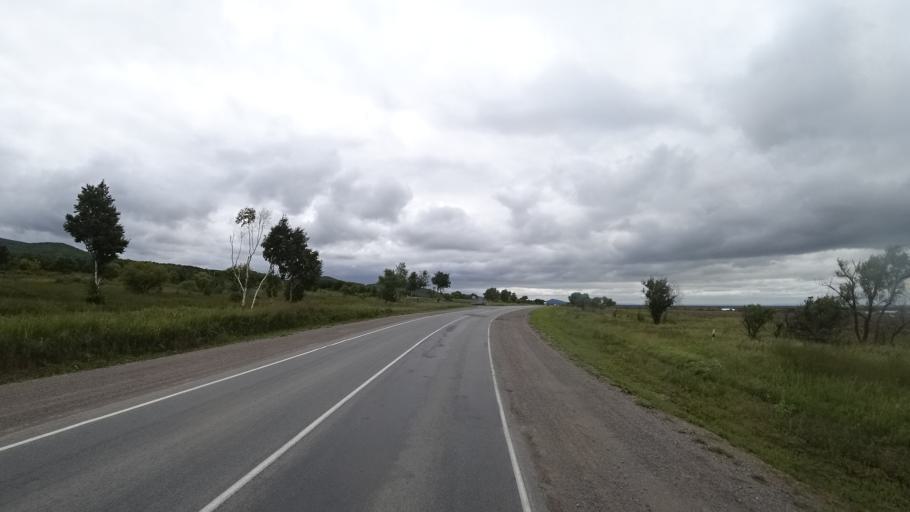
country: RU
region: Primorskiy
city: Chernigovka
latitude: 44.3169
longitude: 132.5629
